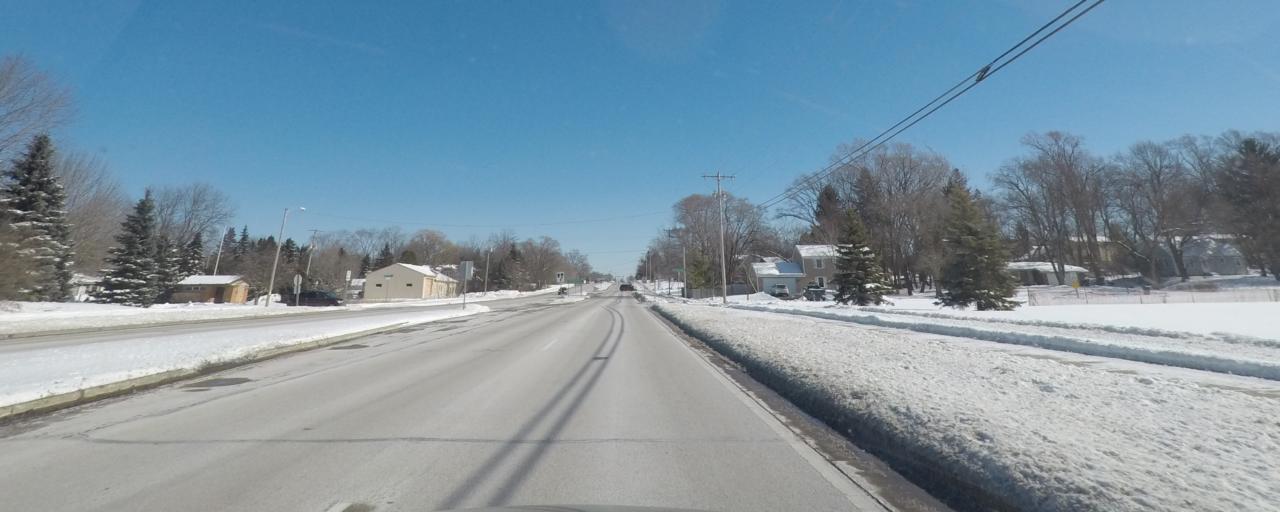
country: US
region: Wisconsin
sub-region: Waukesha County
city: New Berlin
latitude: 43.0169
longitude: -88.1342
